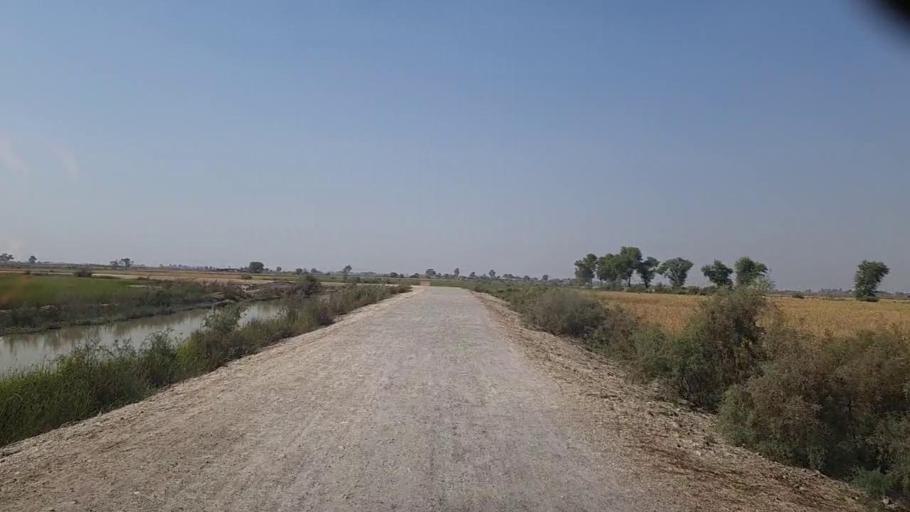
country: PK
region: Sindh
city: Thul
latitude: 28.1768
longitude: 68.7745
